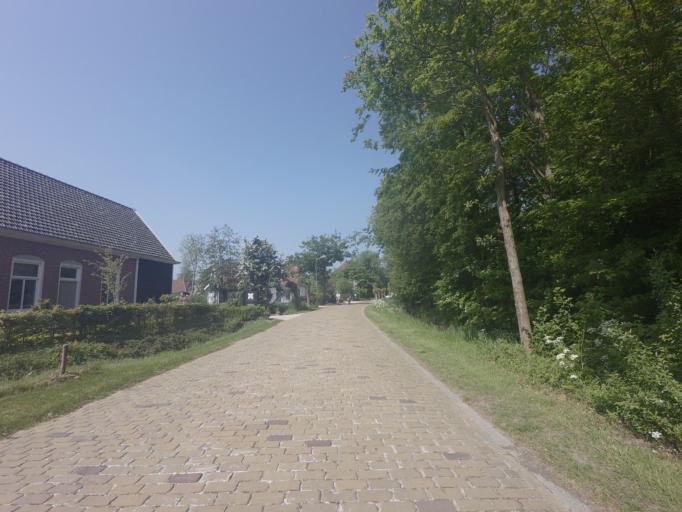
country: NL
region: Zeeland
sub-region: Gemeente Middelburg
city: Middelburg
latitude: 51.5682
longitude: 3.5412
